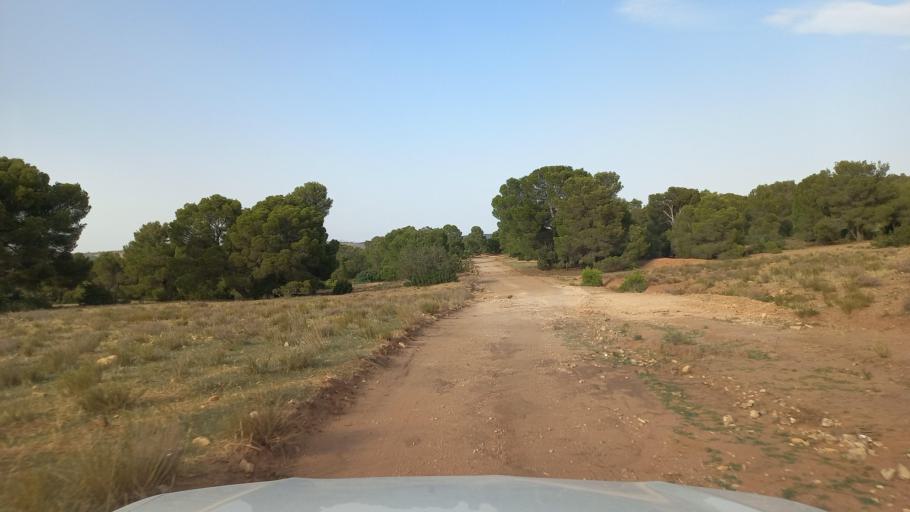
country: TN
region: Al Qasrayn
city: Kasserine
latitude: 35.3397
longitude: 8.8577
